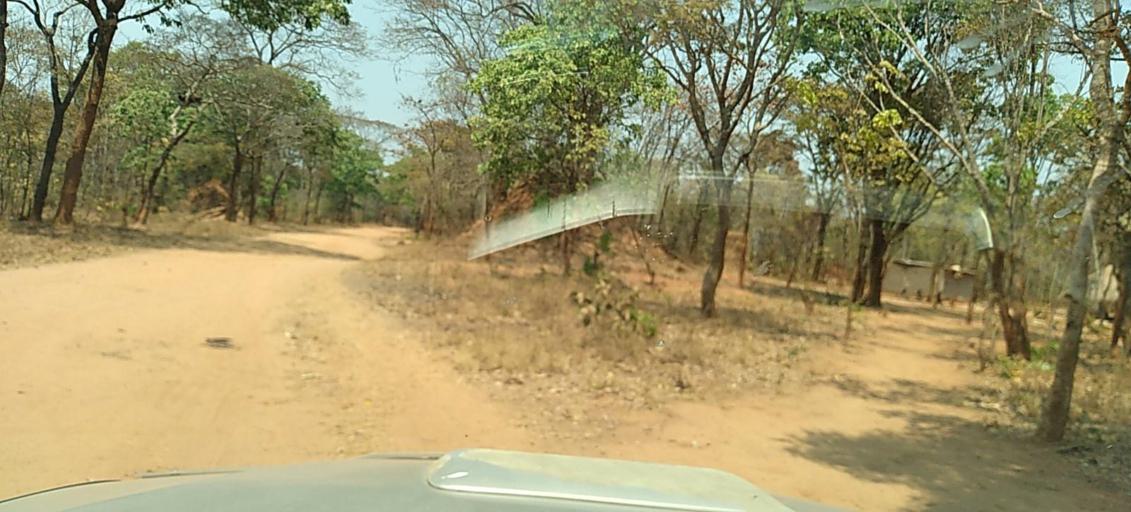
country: ZM
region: North-Western
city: Kasempa
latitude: -13.6688
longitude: 26.2932
